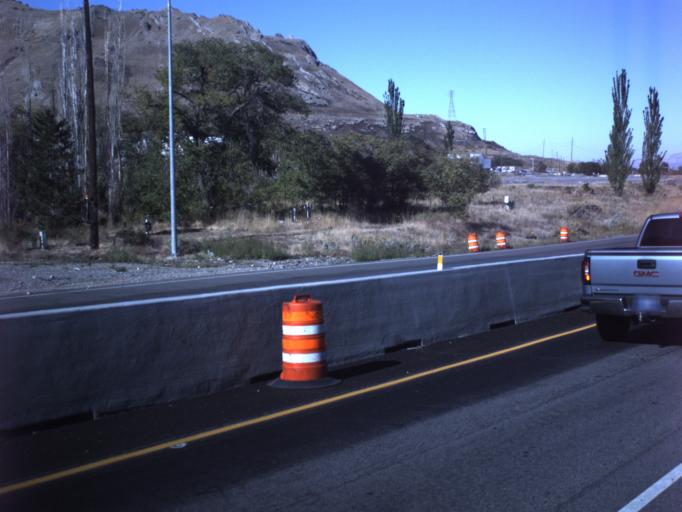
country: US
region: Utah
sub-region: Salt Lake County
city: Magna
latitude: 40.7260
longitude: -112.1624
